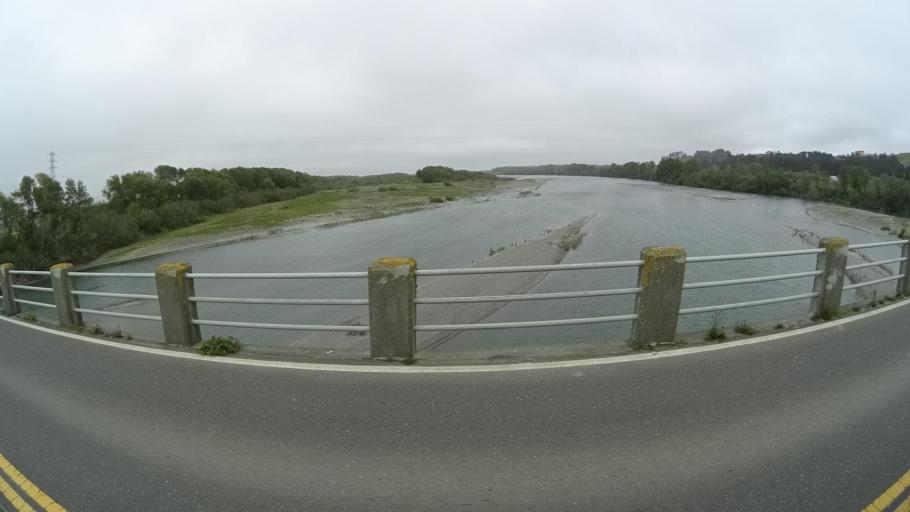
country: US
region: California
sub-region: Humboldt County
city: Fortuna
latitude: 40.6121
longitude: -124.2038
